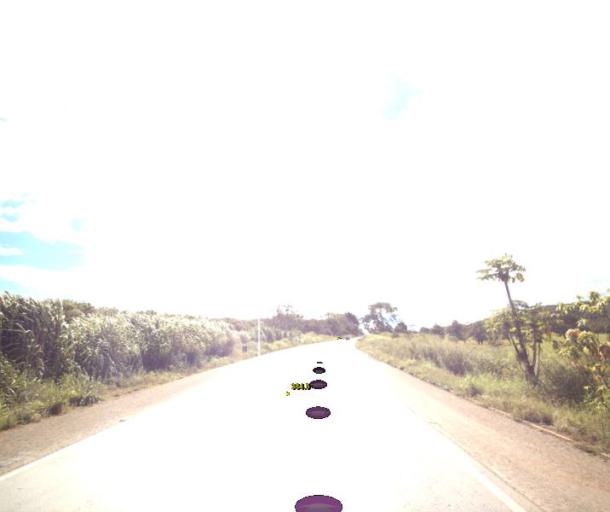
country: BR
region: Goias
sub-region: Petrolina De Goias
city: Petrolina de Goias
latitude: -15.9301
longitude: -49.2082
